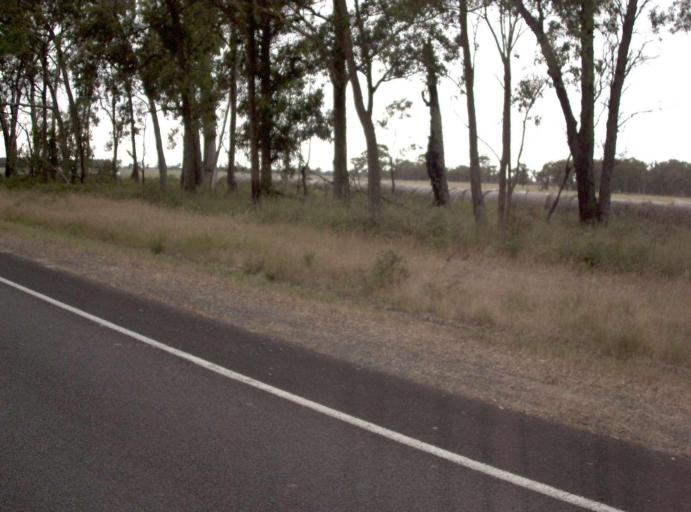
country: AU
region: Victoria
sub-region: Wellington
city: Sale
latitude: -38.4607
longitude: 146.9349
